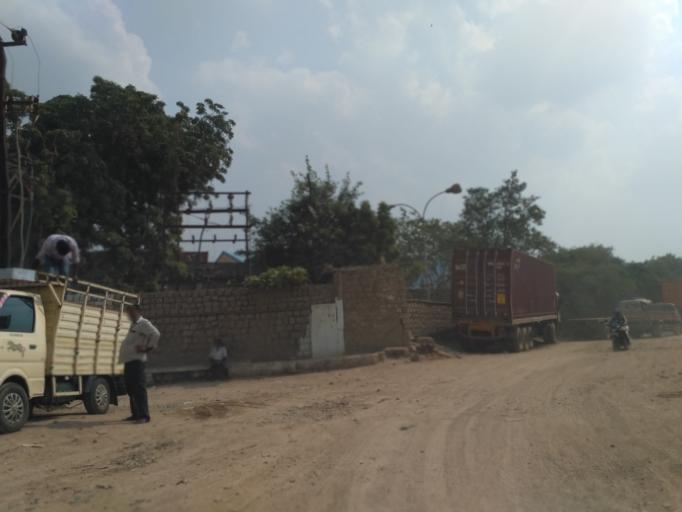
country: IN
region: Telangana
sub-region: Rangareddi
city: Kukatpalli
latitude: 17.4645
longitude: 78.4209
